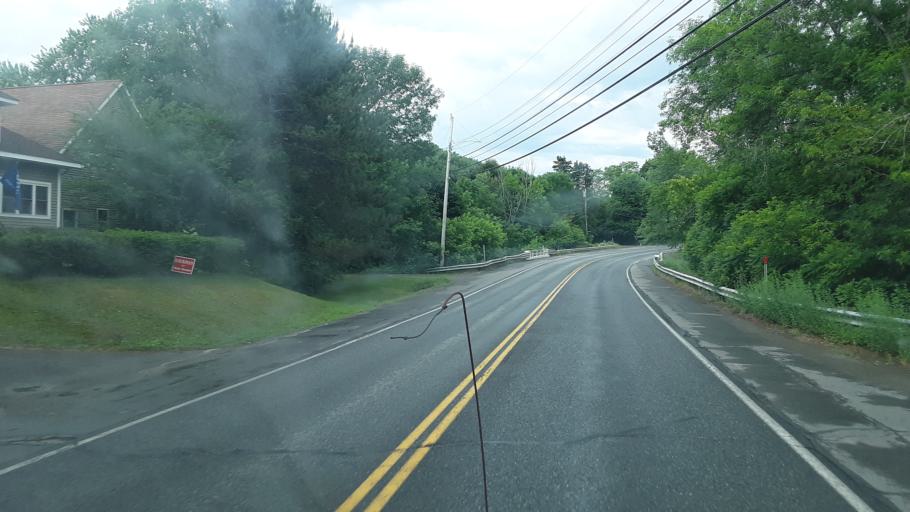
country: US
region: Maine
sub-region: Penobscot County
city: Eddington
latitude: 44.8180
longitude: -68.7065
